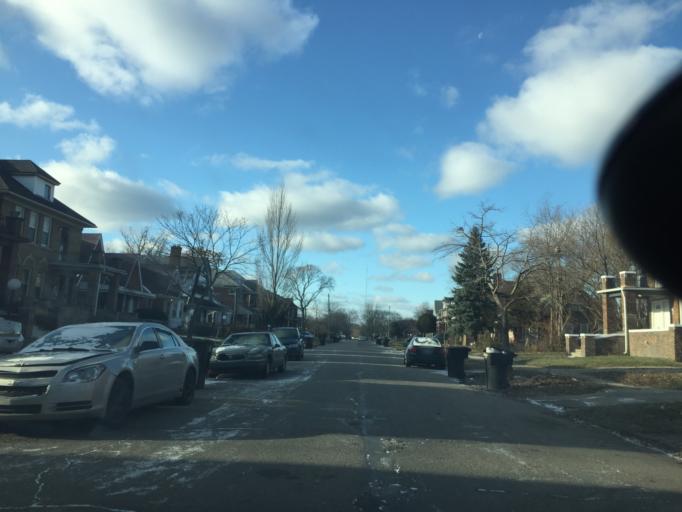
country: US
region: Michigan
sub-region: Wayne County
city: Highland Park
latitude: 42.3953
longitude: -83.1319
